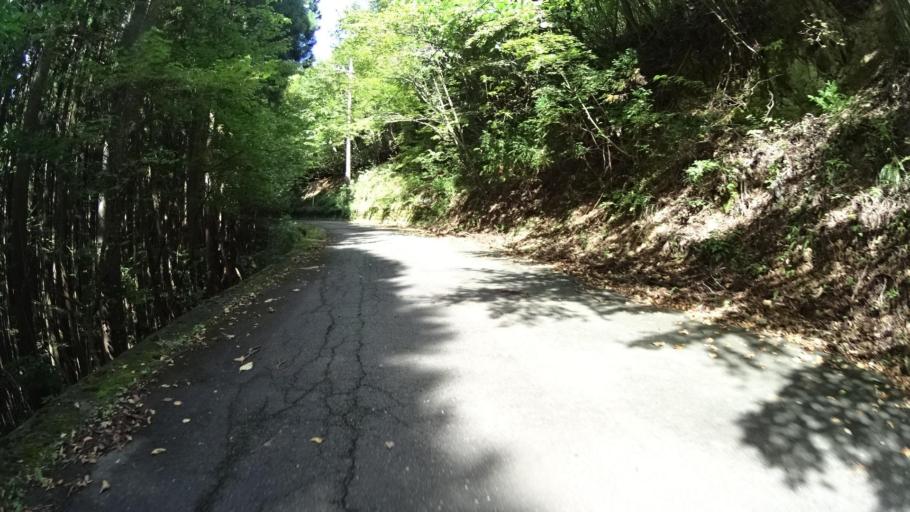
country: JP
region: Yamanashi
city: Uenohara
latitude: 35.7475
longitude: 139.0546
